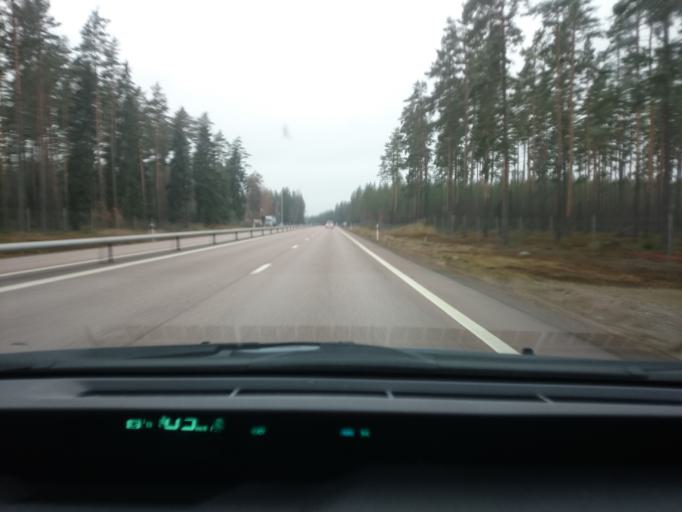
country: SE
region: Dalarna
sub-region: Hedemora Kommun
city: Brunna
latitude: 60.2043
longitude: 16.0832
